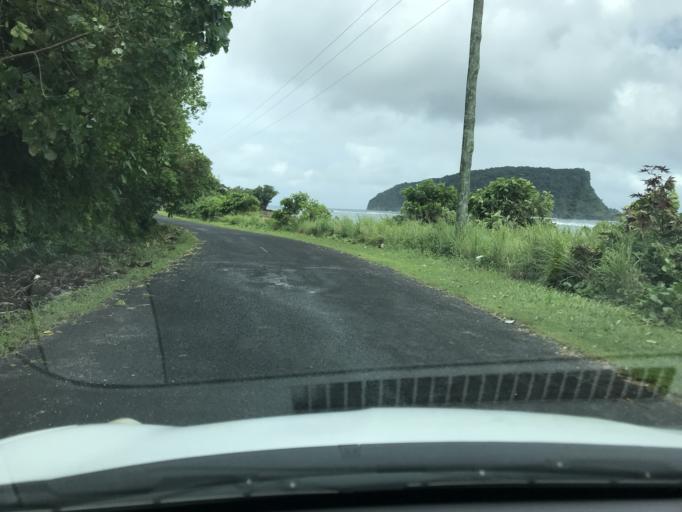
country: WS
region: Va`a-o-Fonoti
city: Samamea
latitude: -14.0468
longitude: -171.4425
